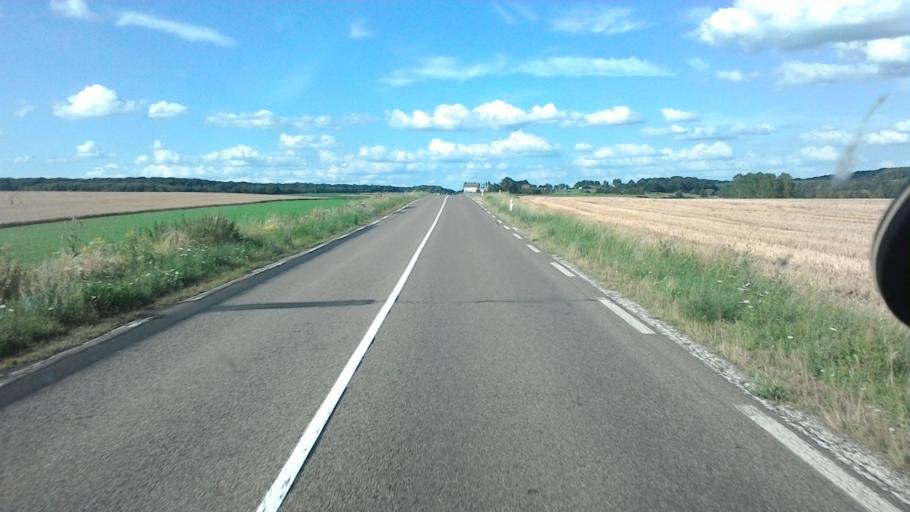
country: FR
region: Franche-Comte
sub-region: Departement de la Haute-Saone
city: Luxeuil-les-Bains
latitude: 47.7240
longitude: 6.3076
